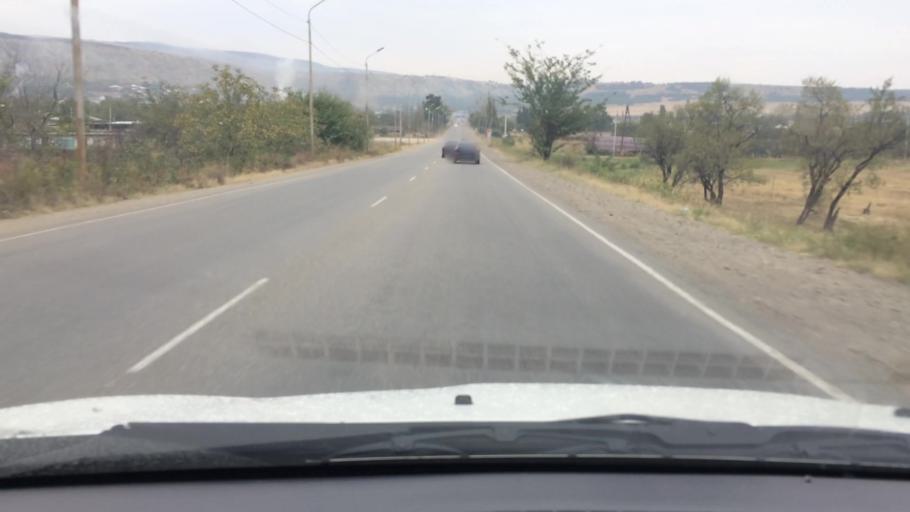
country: GE
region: T'bilisi
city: Tbilisi
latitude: 41.6052
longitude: 44.7822
